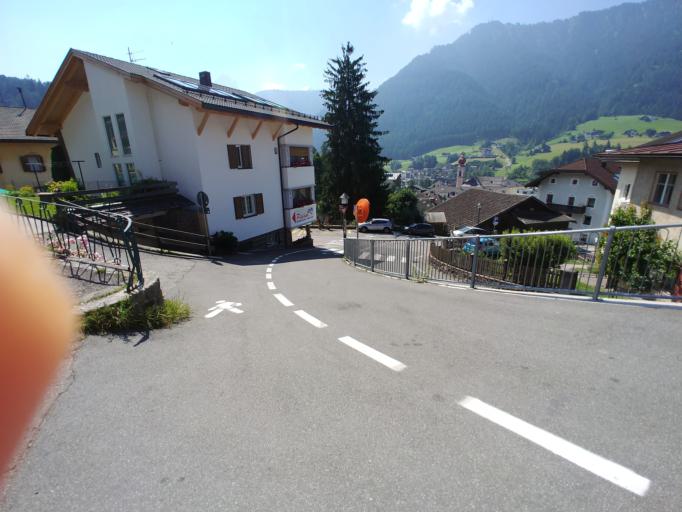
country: IT
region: Trentino-Alto Adige
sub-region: Bolzano
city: Ortisei
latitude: 46.5779
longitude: 11.6723
